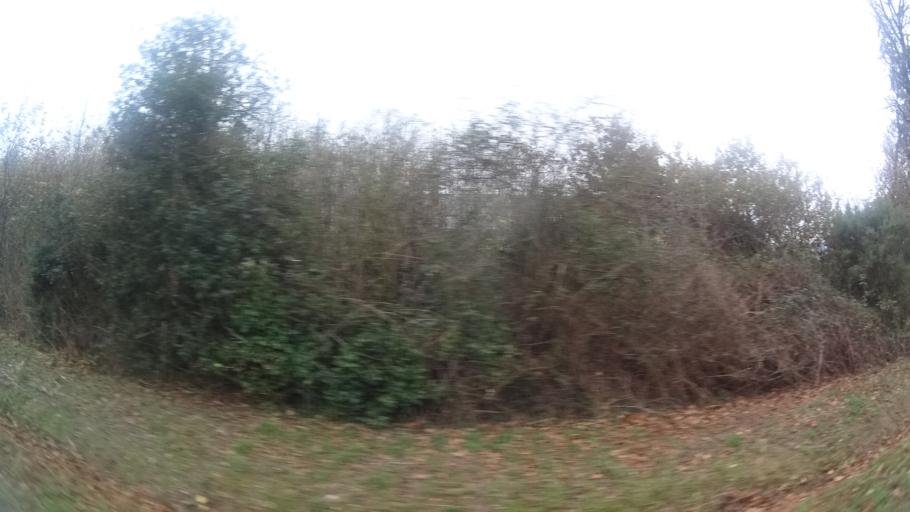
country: FR
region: Brittany
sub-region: Departement d'Ille-et-Vilaine
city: Bains-sur-Oust
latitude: 47.6828
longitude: -2.0478
